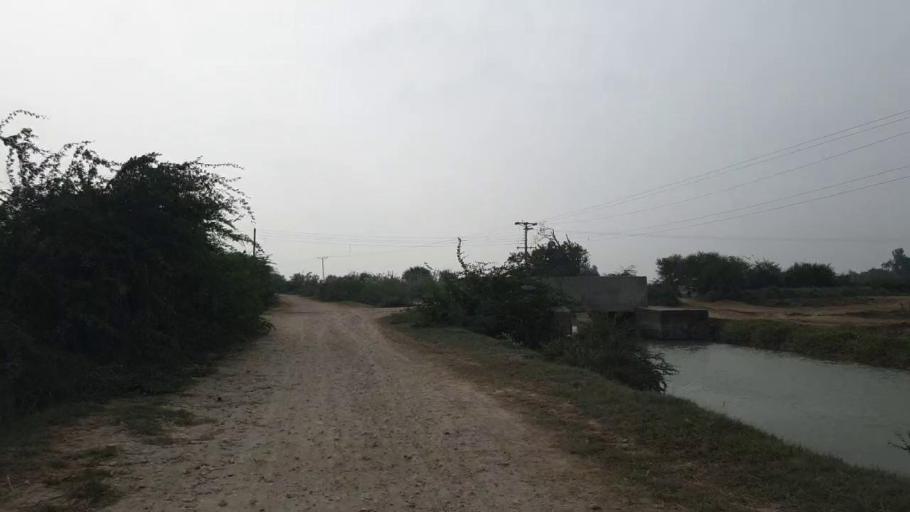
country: PK
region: Sindh
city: Kario
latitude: 24.8644
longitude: 68.5185
